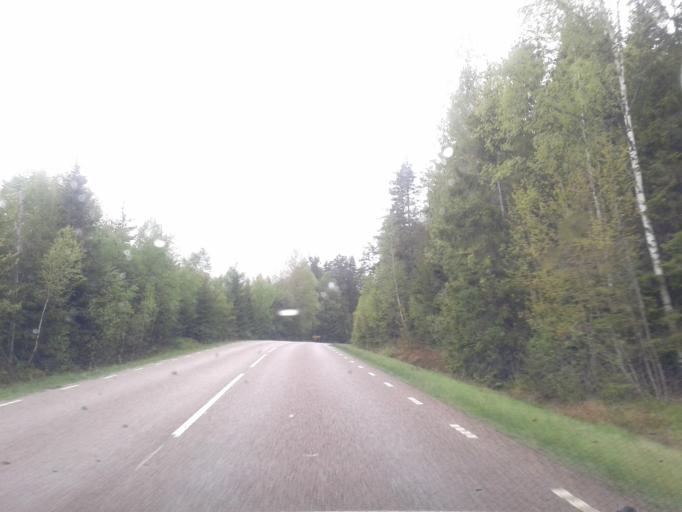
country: SE
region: Vaestra Goetaland
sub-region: Lilla Edets Kommun
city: Lodose
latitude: 58.0796
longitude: 12.1210
